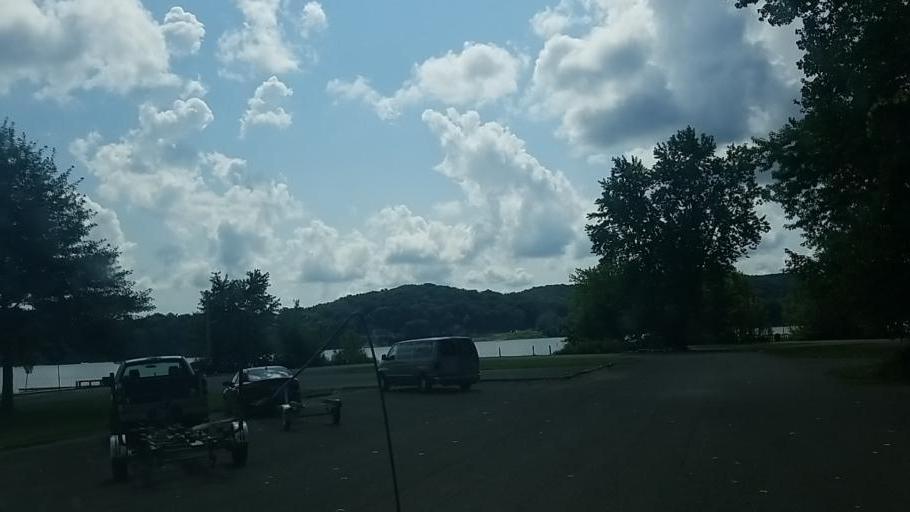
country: US
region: Ohio
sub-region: Ashland County
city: Loudonville
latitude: 40.6437
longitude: -82.3456
